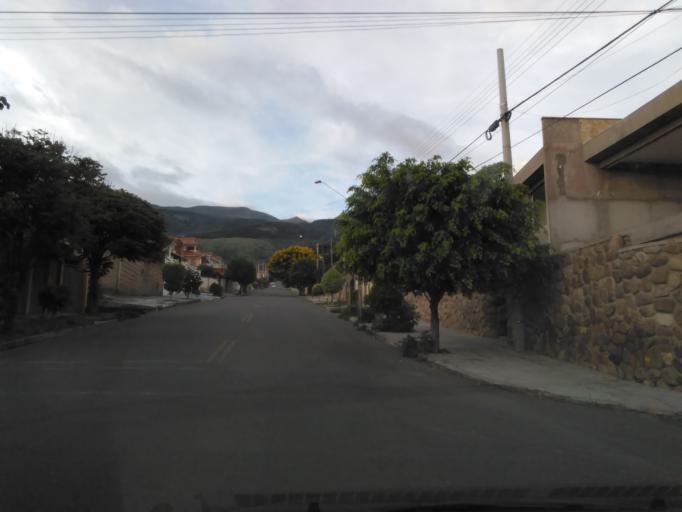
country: BO
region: Cochabamba
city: Cochabamba
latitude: -17.3618
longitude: -66.1564
